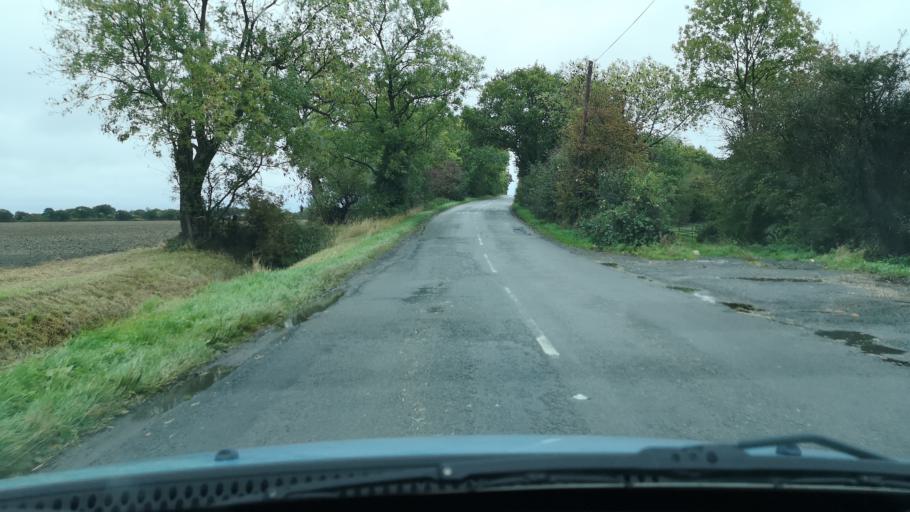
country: GB
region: England
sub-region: Doncaster
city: Moss
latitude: 53.6199
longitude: -1.0732
